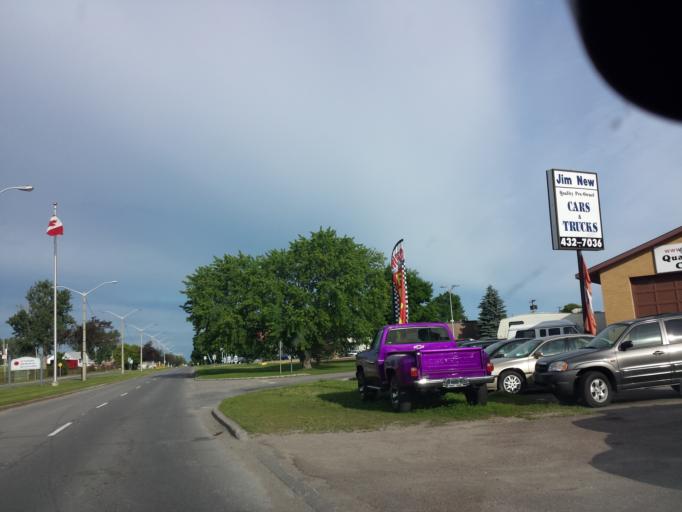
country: CA
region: Ontario
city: Renfrew
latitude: 45.4691
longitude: -76.6705
